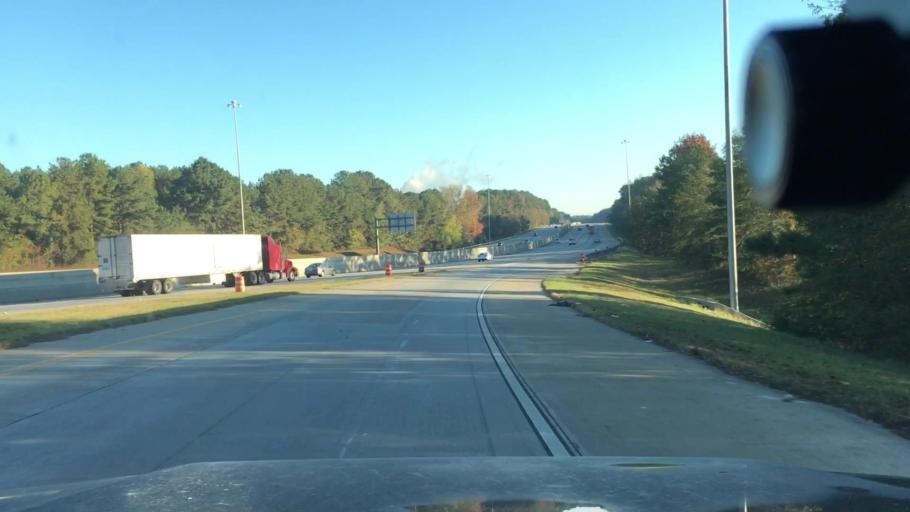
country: US
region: Georgia
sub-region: Fulton County
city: Palmetto
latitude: 33.4441
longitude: -84.6913
